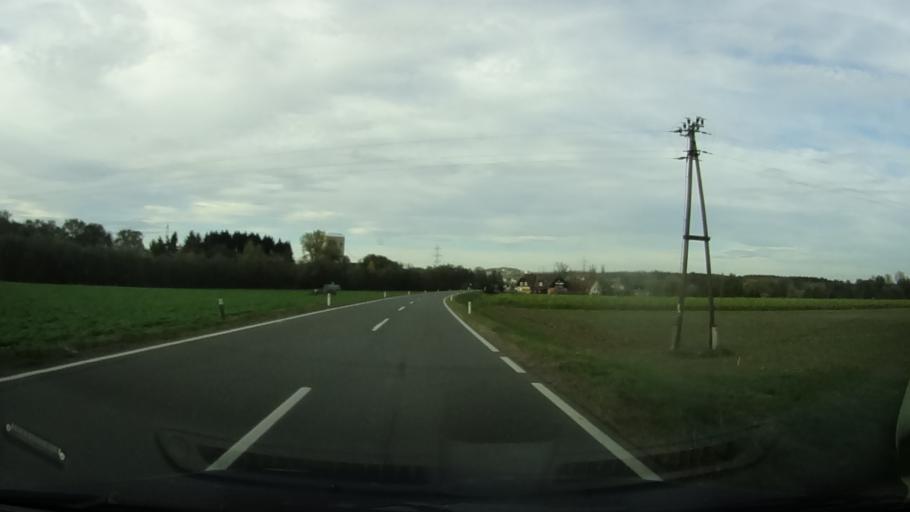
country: AT
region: Styria
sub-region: Politischer Bezirk Deutschlandsberg
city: Preding
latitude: 46.8420
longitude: 15.4111
